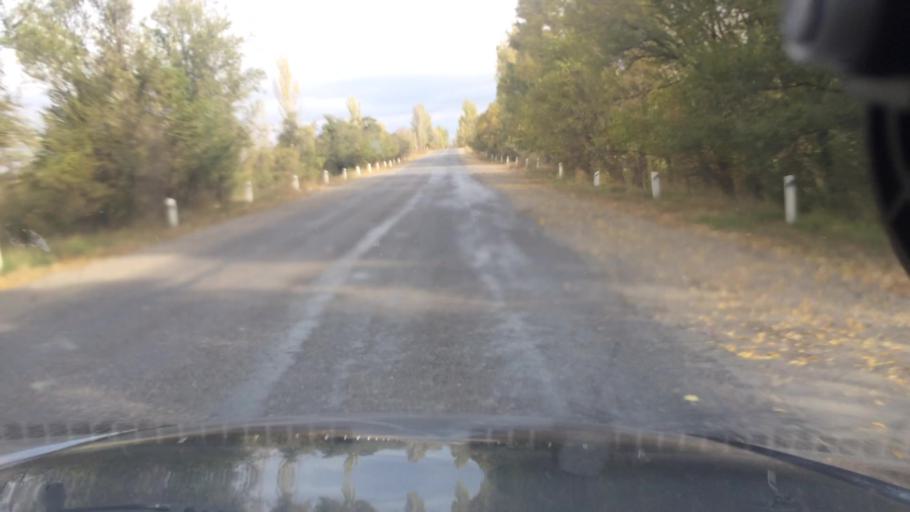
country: KG
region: Ysyk-Koel
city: Karakol
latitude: 42.5664
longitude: 78.3912
